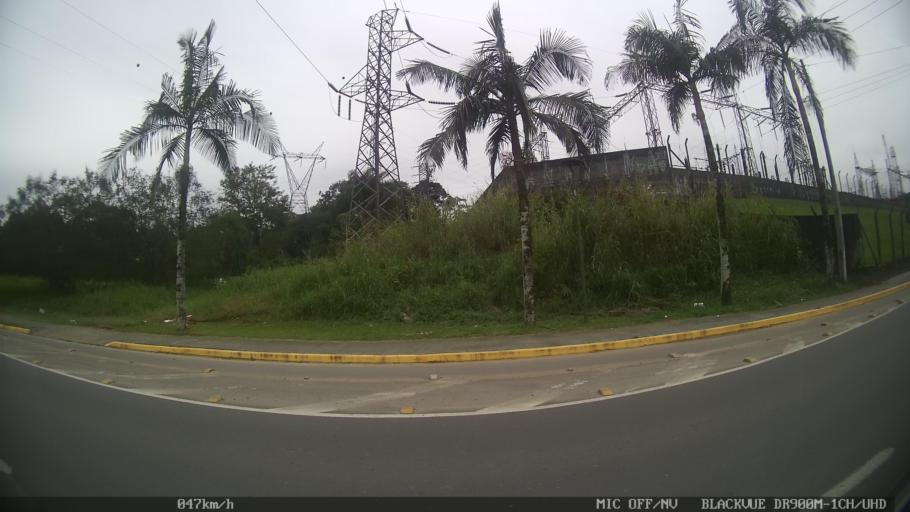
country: BR
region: Santa Catarina
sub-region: Joinville
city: Joinville
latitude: -26.2920
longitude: -48.8891
